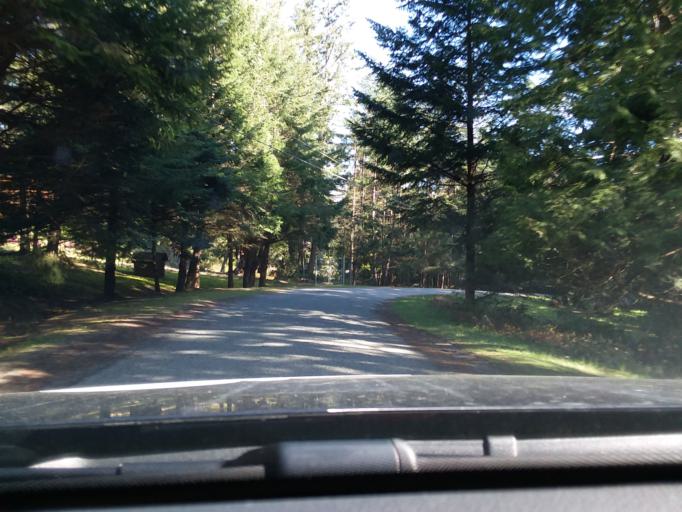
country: CA
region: British Columbia
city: North Saanich
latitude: 48.8745
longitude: -123.3260
